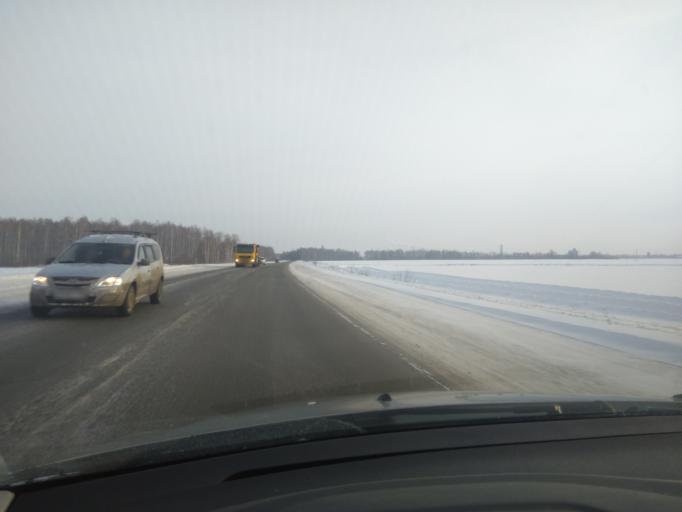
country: RU
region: Sverdlovsk
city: Bogdanovich
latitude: 56.7980
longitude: 62.0086
